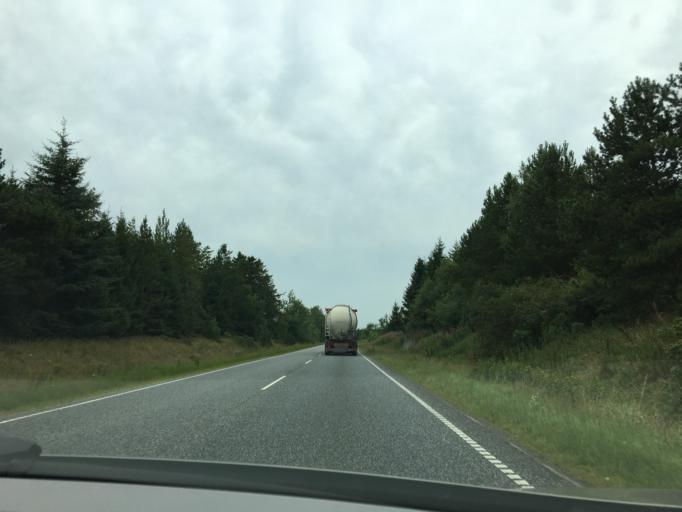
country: DK
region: Central Jutland
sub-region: Herning Kommune
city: Sunds
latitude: 56.3074
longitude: 8.9986
